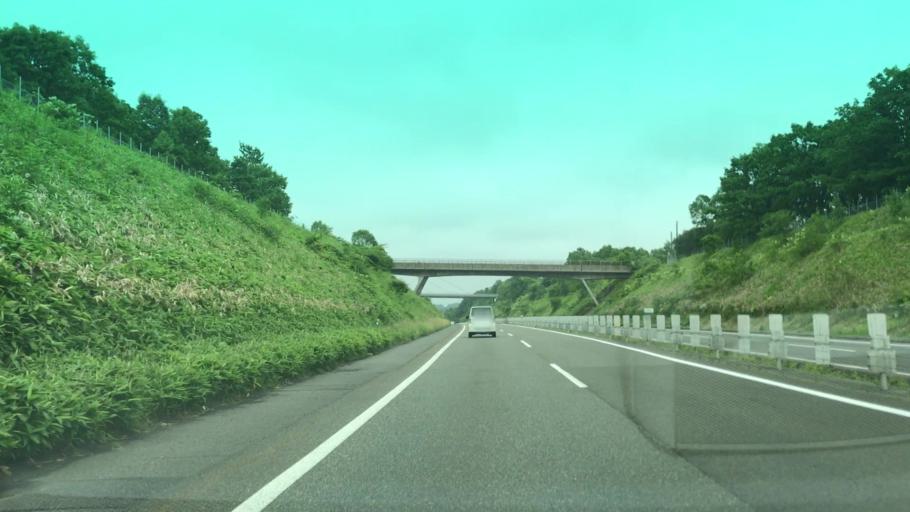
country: JP
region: Hokkaido
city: Tomakomai
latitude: 42.6204
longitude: 141.4769
